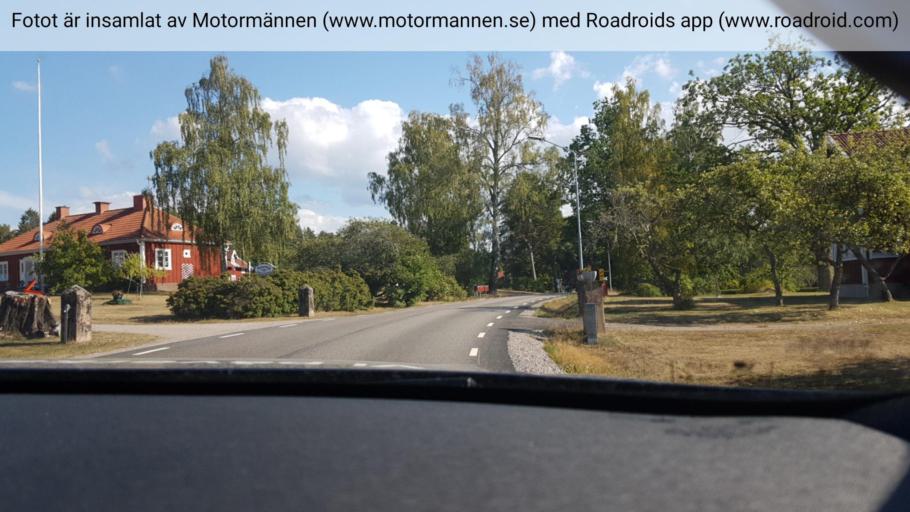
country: SE
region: Vaestra Goetaland
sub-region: Gotene Kommun
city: Goetene
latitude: 58.6362
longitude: 13.5617
